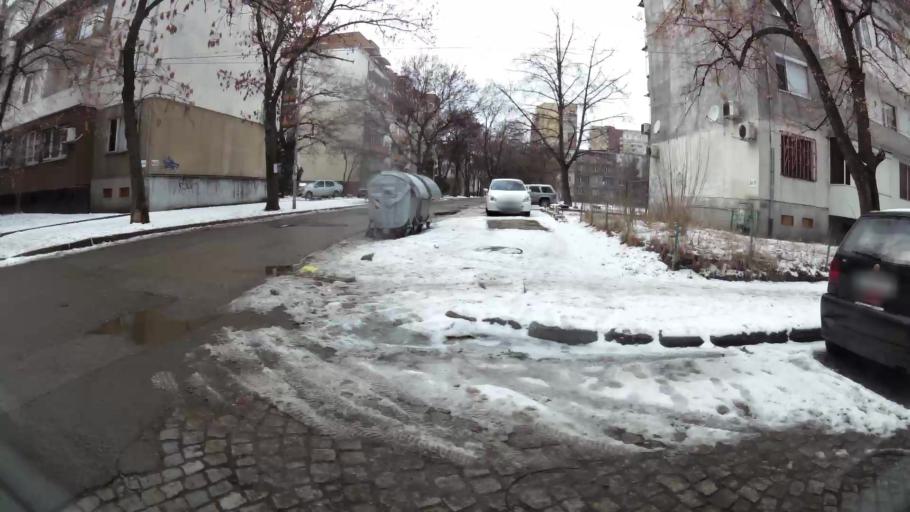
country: BG
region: Sofia-Capital
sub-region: Stolichna Obshtina
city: Sofia
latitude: 42.7025
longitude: 23.3677
